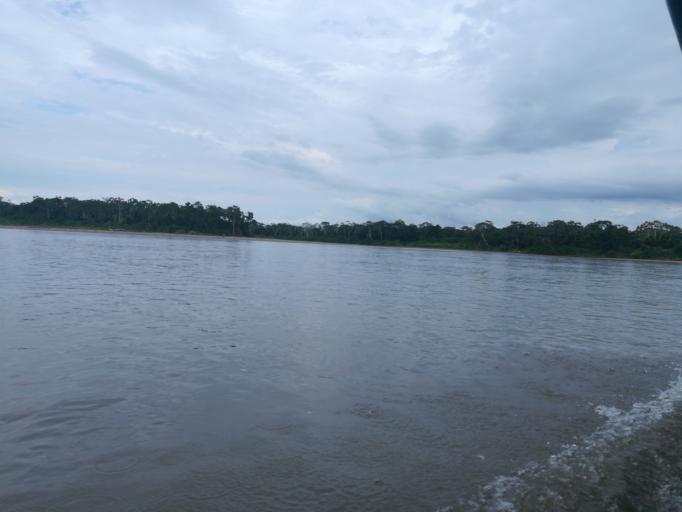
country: EC
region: Orellana
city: Boca Suno
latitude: -0.7609
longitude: -77.1562
